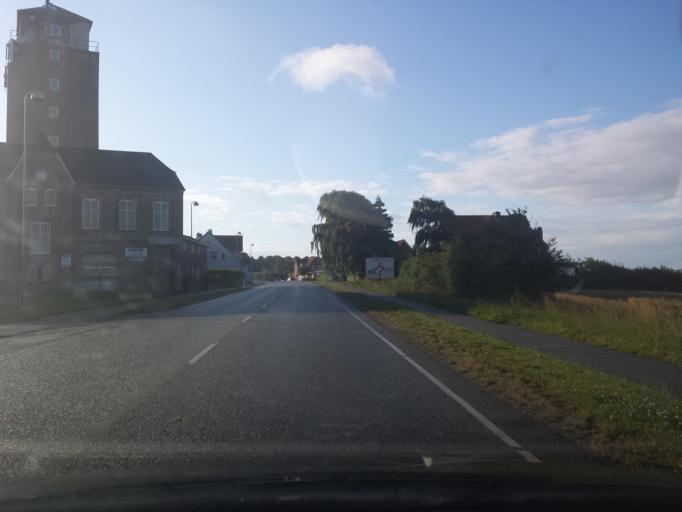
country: DK
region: South Denmark
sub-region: Sonderborg Kommune
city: Broager
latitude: 54.9209
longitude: 9.6789
